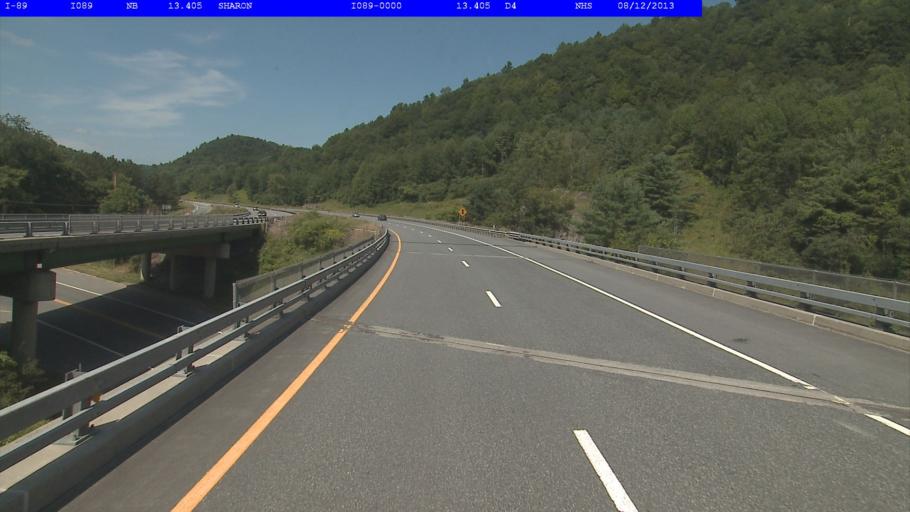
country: US
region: Vermont
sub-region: Windsor County
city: Woodstock
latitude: 43.7863
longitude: -72.4520
